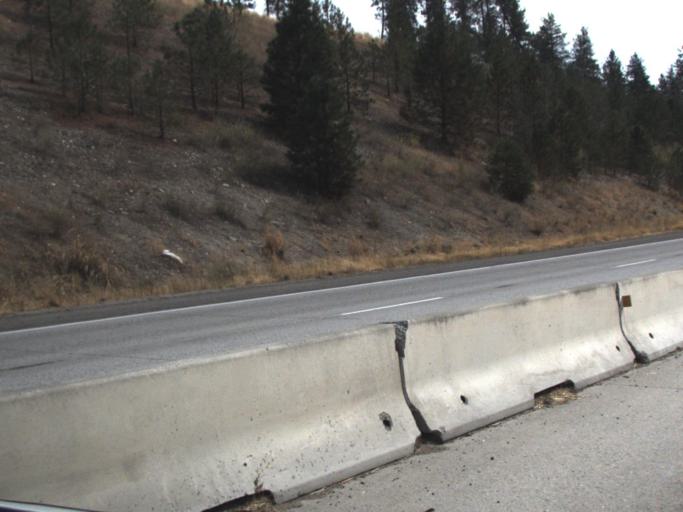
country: US
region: Washington
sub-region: Spokane County
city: Fairwood
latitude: 47.7894
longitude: -117.4084
